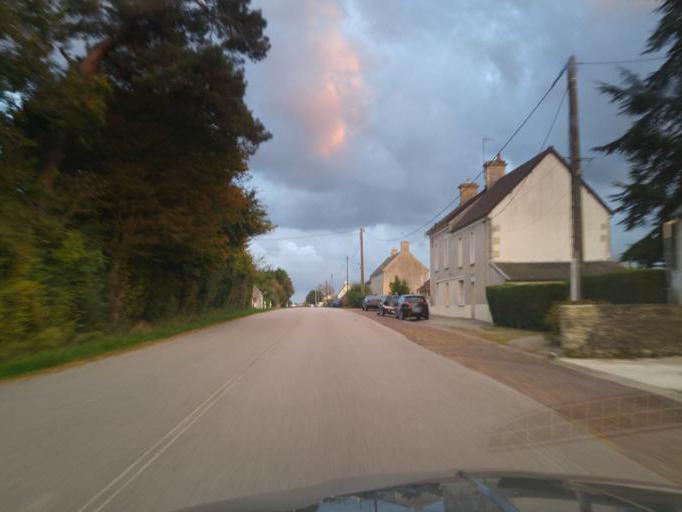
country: FR
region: Lower Normandy
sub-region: Departement du Calvados
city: Grandcamp-Maisy
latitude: 49.3423
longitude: -1.0003
